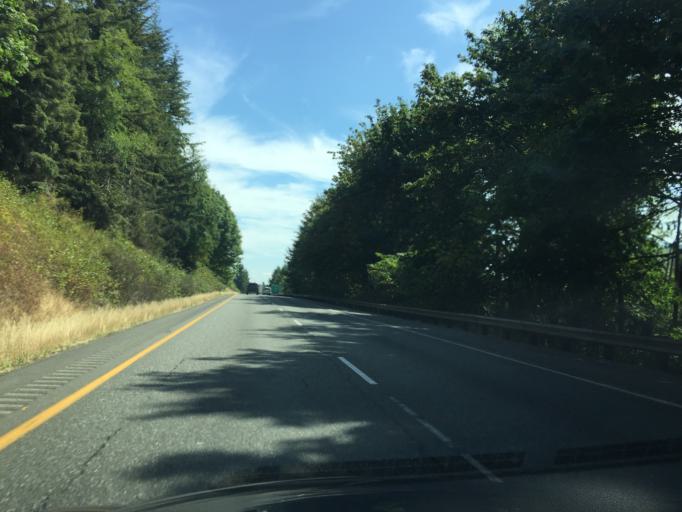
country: US
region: Washington
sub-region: Whatcom County
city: Sudden Valley
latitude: 48.6600
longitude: -122.3710
